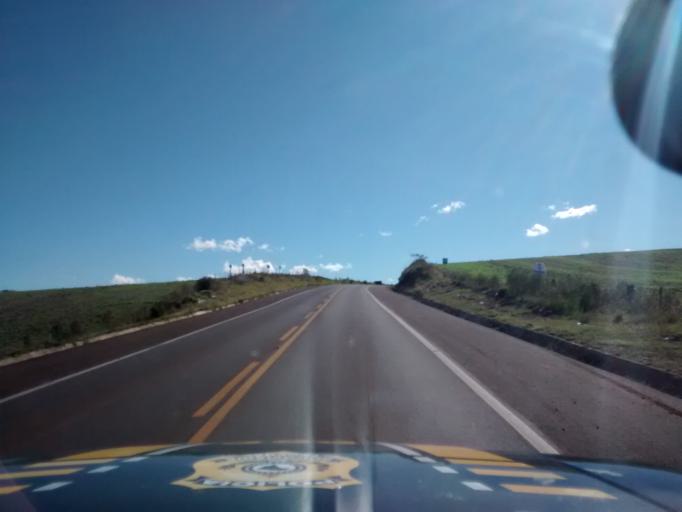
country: BR
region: Rio Grande do Sul
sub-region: Lagoa Vermelha
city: Lagoa Vermelha
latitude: -28.3167
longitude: -51.3560
